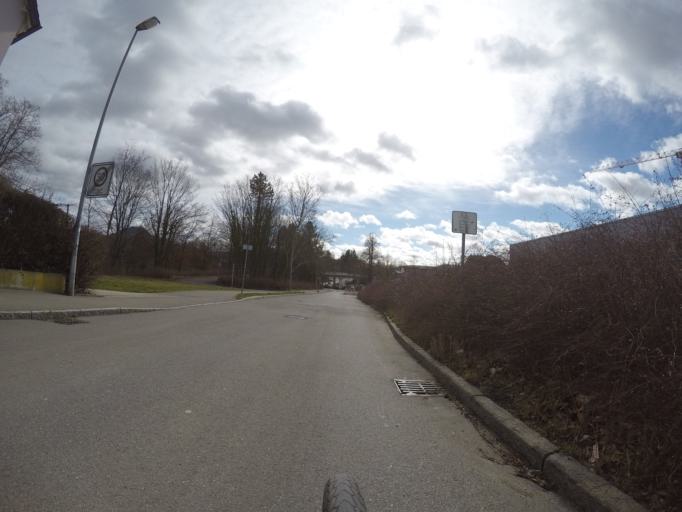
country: DE
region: Baden-Wuerttemberg
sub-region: Tuebingen Region
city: Reutlingen
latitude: 48.5025
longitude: 9.2012
